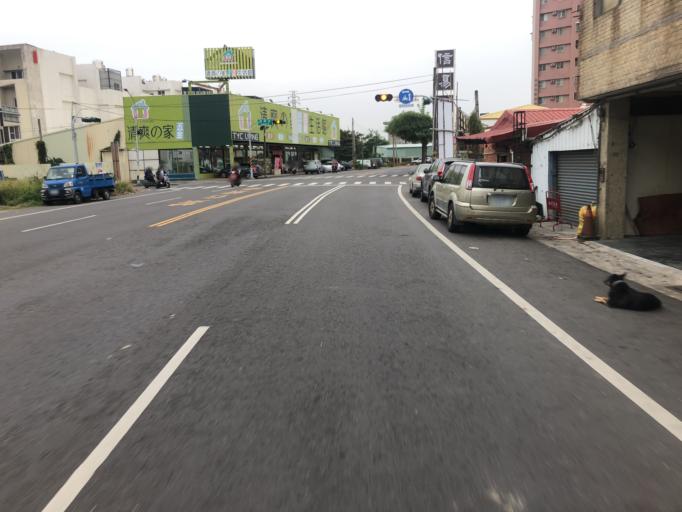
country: TW
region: Taiwan
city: Xinying
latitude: 23.1792
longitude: 120.2478
